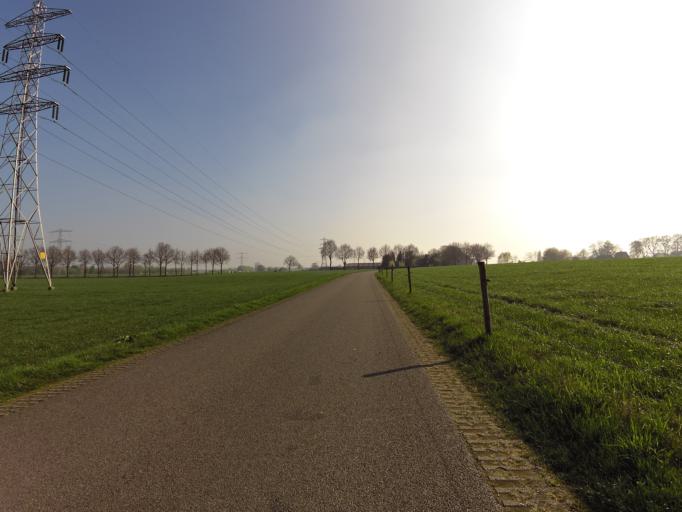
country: NL
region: Gelderland
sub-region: Gemeente Bronckhorst
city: Baak
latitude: 52.0552
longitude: 6.2511
